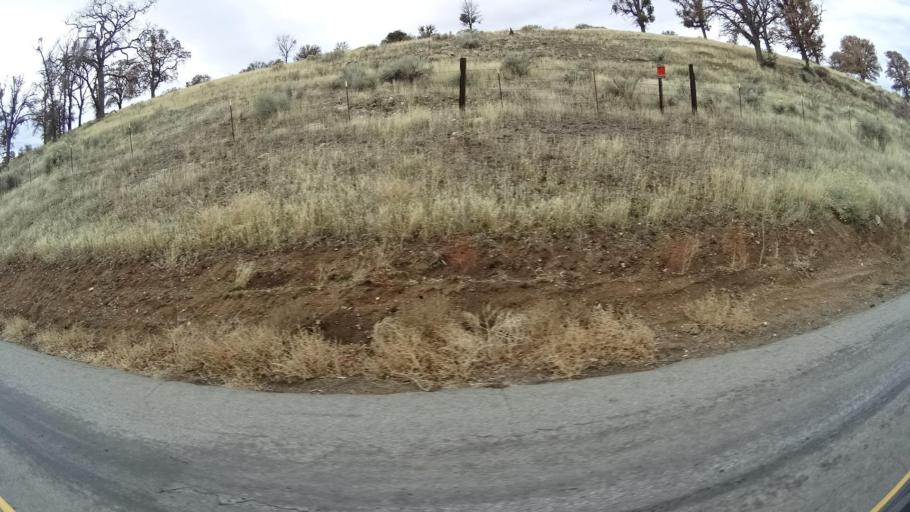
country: US
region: California
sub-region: Kern County
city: Golden Hills
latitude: 35.1253
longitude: -118.5544
